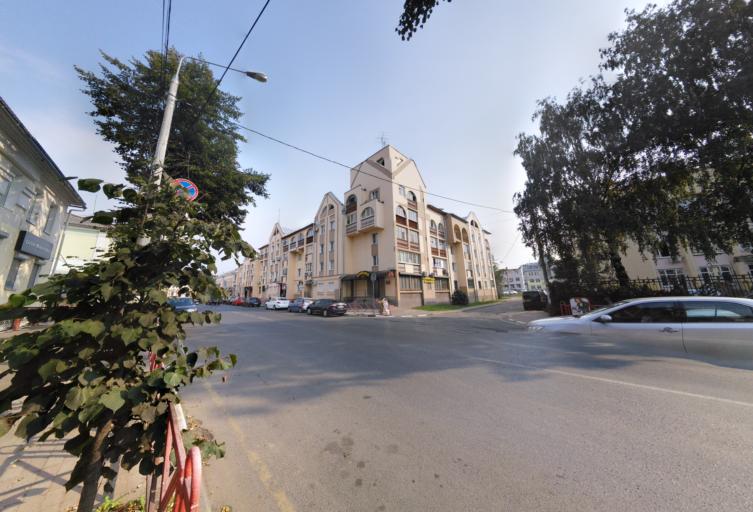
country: RU
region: Jaroslavl
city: Yaroslavl
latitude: 57.6242
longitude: 39.8814
